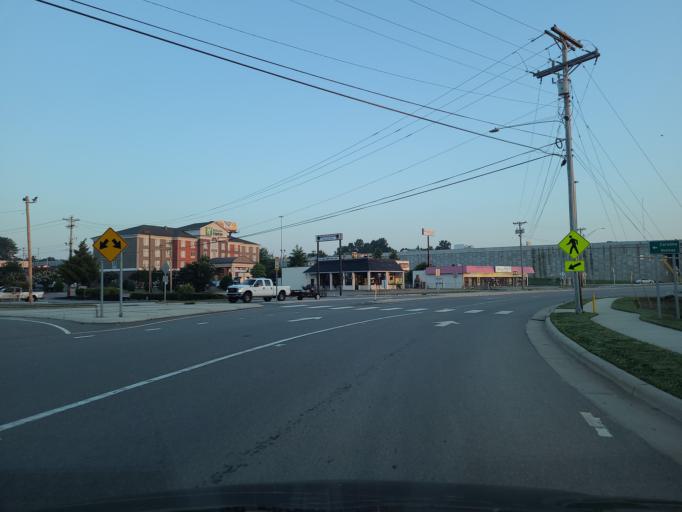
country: US
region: North Carolina
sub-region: Iredell County
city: Statesville
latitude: 35.8055
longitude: -80.8758
